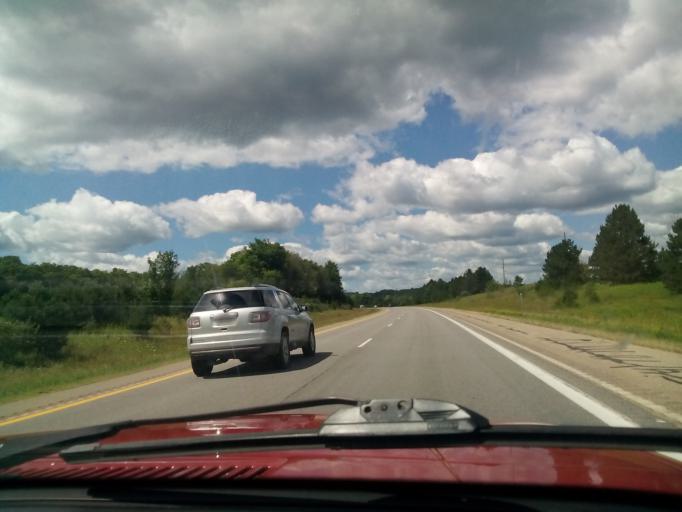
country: US
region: Michigan
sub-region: Ogemaw County
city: West Branch
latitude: 44.2574
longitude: -84.2490
